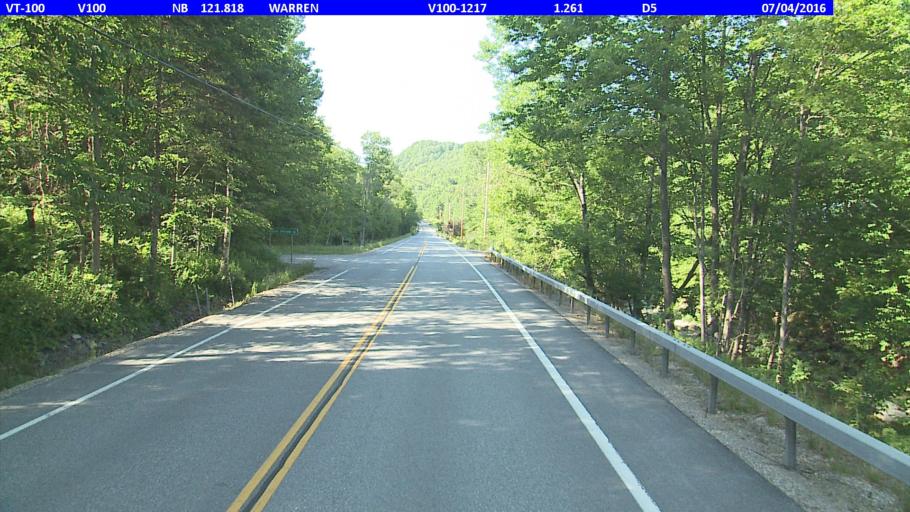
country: US
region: Vermont
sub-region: Washington County
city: Northfield
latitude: 44.0776
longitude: -72.8592
